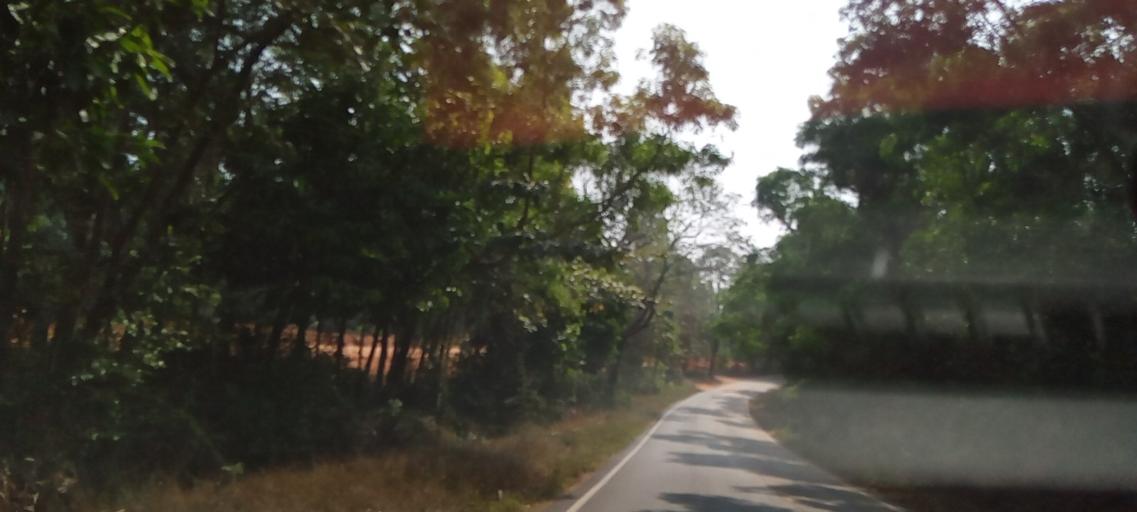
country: IN
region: Karnataka
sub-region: Udupi
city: Manipala
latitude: 13.5131
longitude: 74.8090
